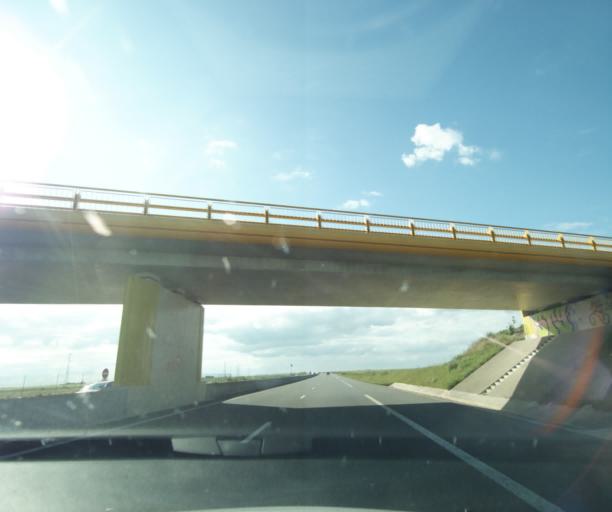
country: FR
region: Centre
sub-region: Departement d'Eure-et-Loir
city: Sours
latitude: 48.3471
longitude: 1.6271
